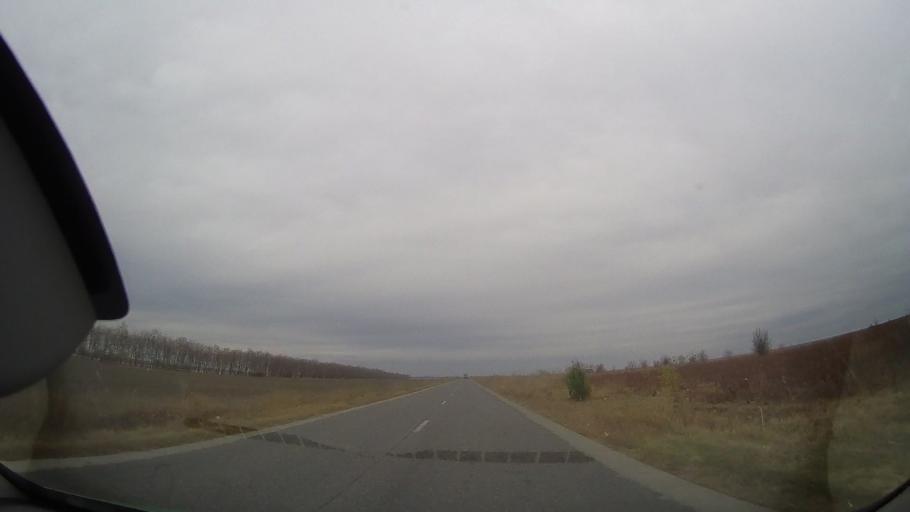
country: RO
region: Ialomita
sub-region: Comuna Milosesti
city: Milosesti
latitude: 44.7455
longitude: 27.2450
